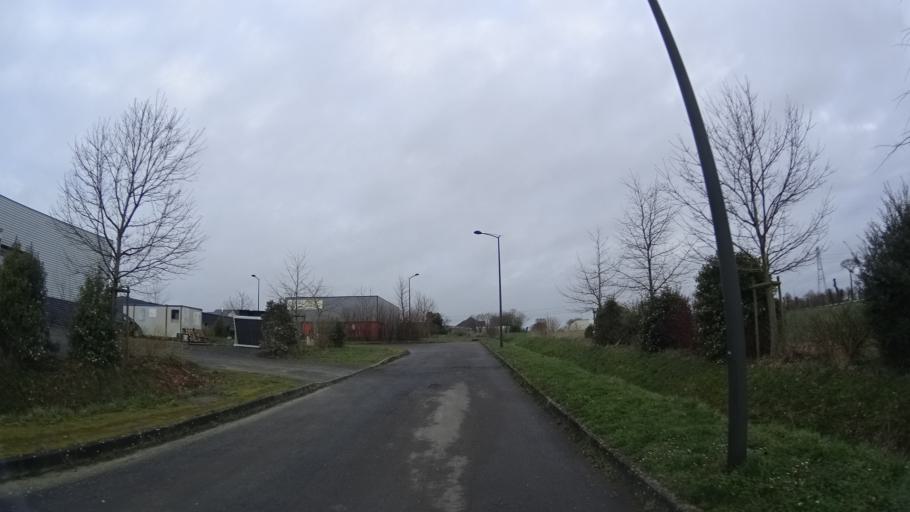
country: FR
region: Brittany
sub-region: Departement d'Ille-et-Vilaine
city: Romille
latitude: 48.2213
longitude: -1.8890
